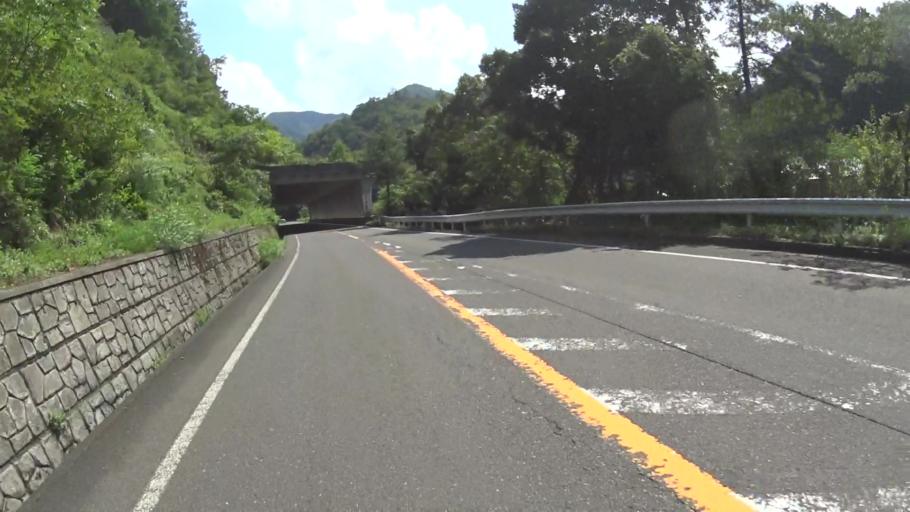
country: JP
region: Fukui
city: Obama
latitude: 35.3943
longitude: 135.5836
